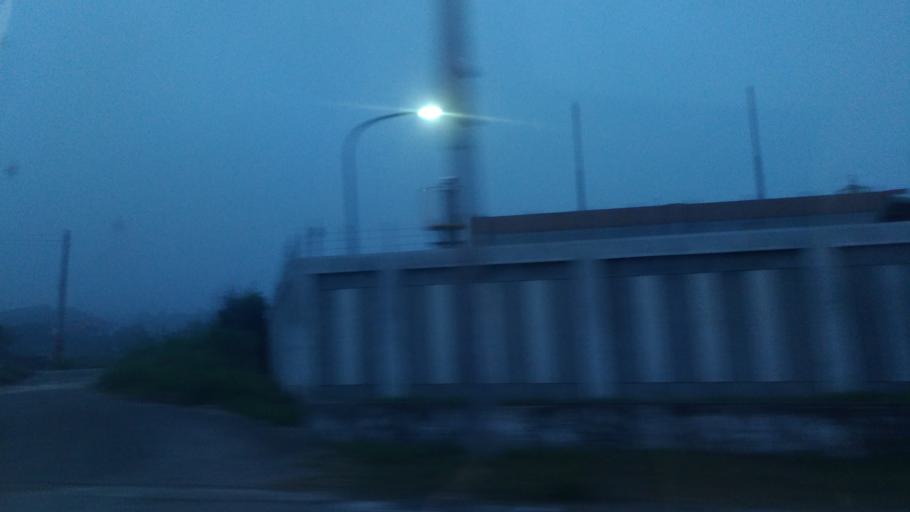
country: TW
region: Taiwan
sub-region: Miaoli
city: Miaoli
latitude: 24.5573
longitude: 120.7053
